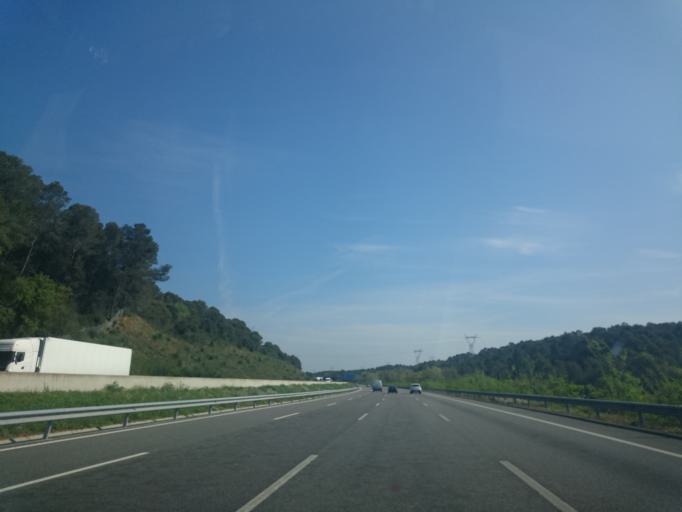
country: ES
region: Catalonia
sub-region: Provincia de Girona
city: Celra
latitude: 42.0577
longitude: 2.8831
